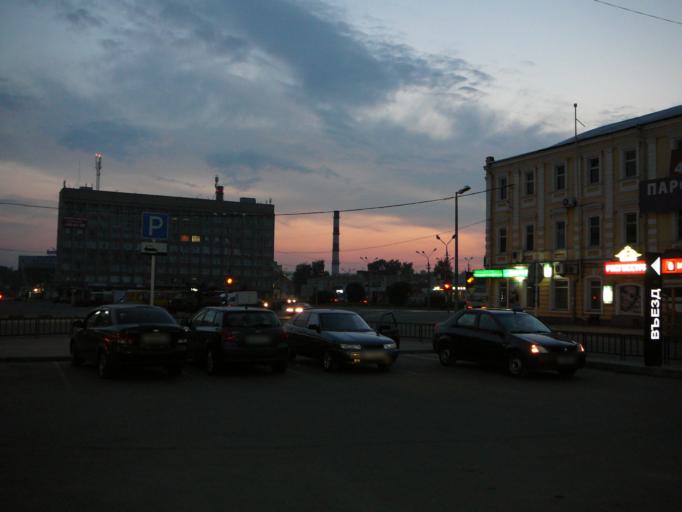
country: RU
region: Smolensk
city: Smolensk
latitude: 54.7953
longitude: 32.0447
